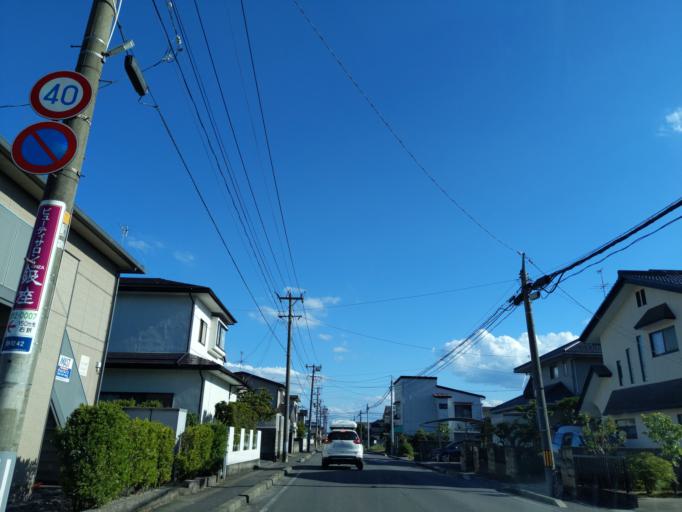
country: JP
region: Fukushima
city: Koriyama
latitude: 37.3880
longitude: 140.3353
